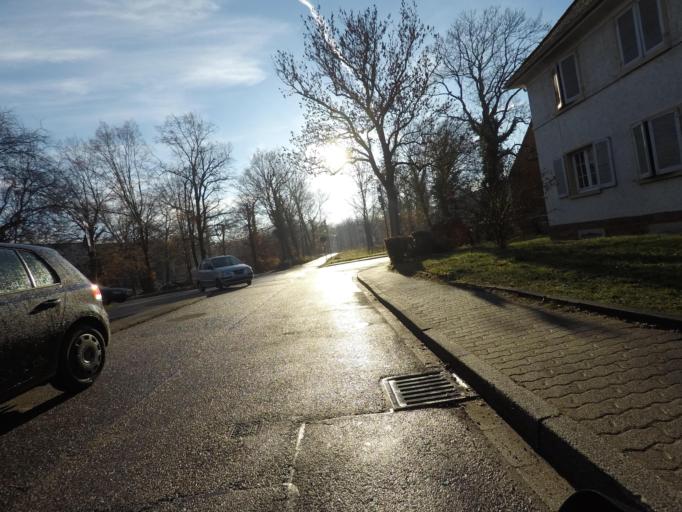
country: DE
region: Baden-Wuerttemberg
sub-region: Karlsruhe Region
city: Karlsruhe
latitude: 48.9755
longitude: 8.4117
